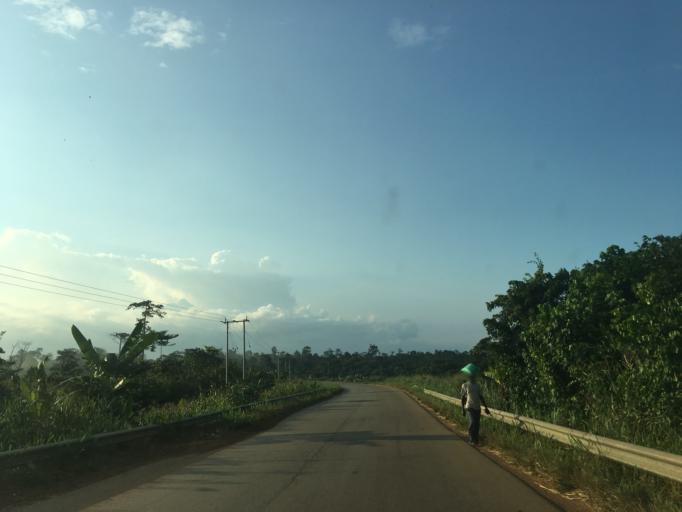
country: GH
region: Western
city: Bibiani
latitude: 6.5721
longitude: -2.3720
